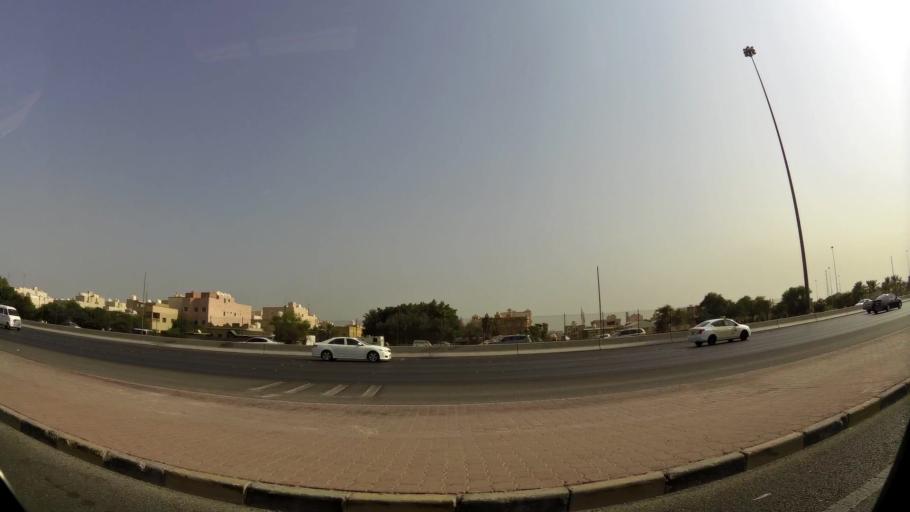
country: KW
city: Bayan
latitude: 29.3165
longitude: 48.0552
